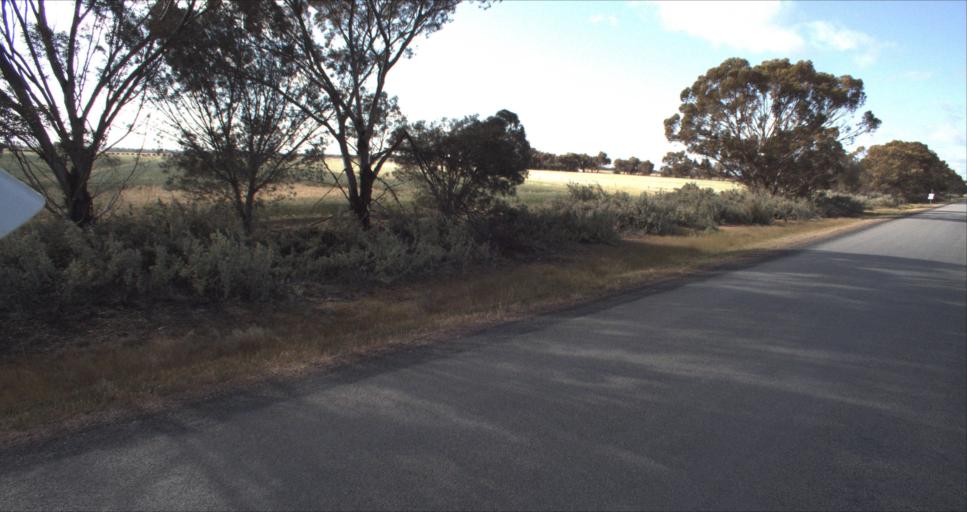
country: AU
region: New South Wales
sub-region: Leeton
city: Leeton
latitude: -34.5051
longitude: 146.3933
